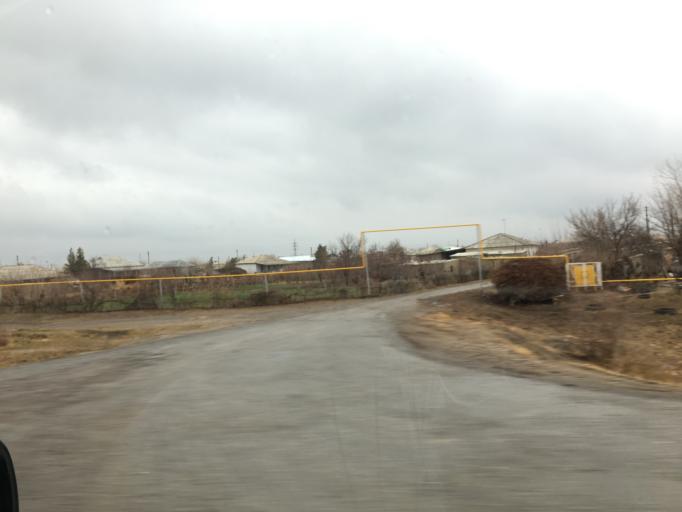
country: TM
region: Mary
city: Yoloeten
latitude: 37.3057
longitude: 62.3238
